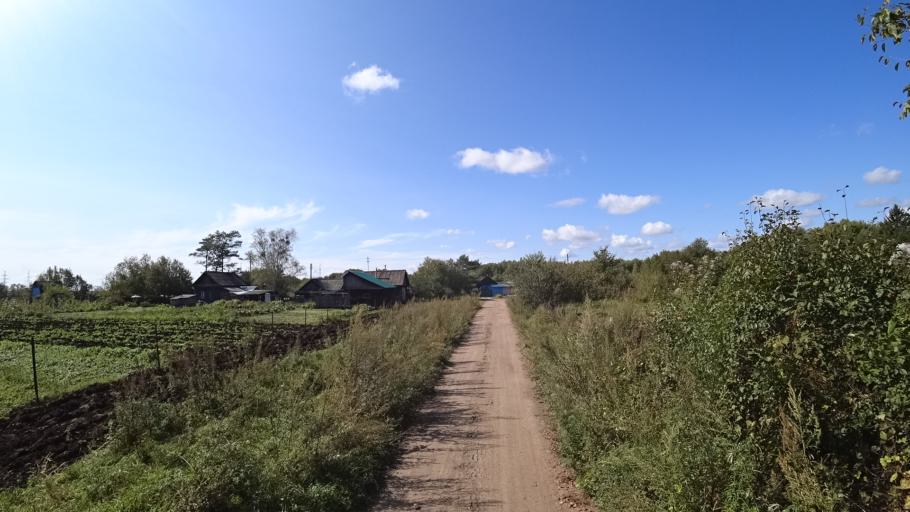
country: RU
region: Amur
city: Arkhara
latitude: 49.3992
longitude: 130.1271
